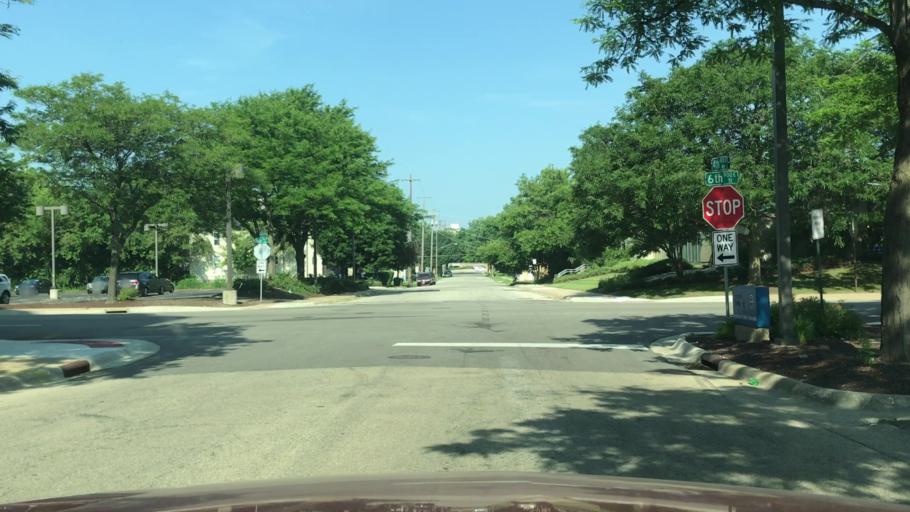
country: US
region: Illinois
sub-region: Winnebago County
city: Rockford
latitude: 42.2627
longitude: -89.0818
